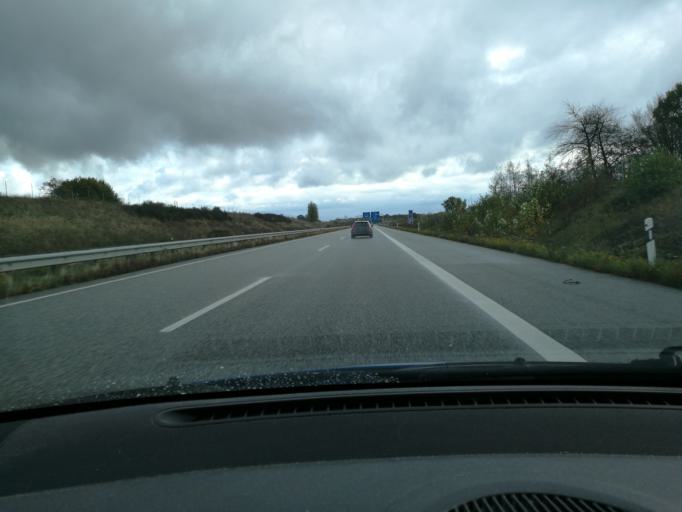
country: DE
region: Schleswig-Holstein
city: Badendorf
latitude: 53.8564
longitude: 10.5797
